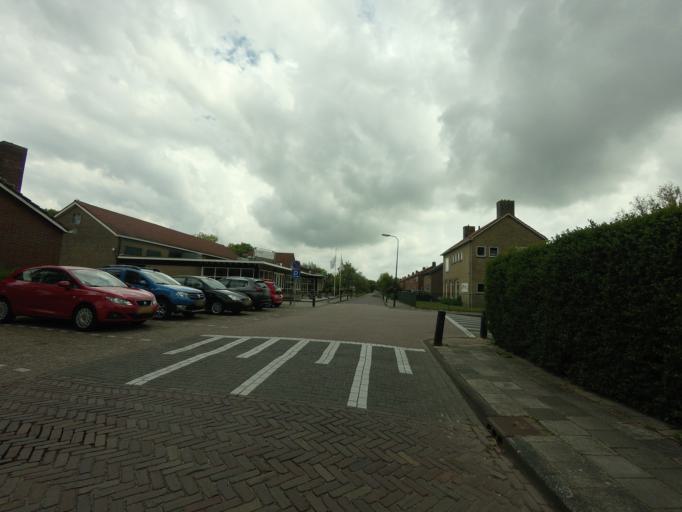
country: NL
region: Friesland
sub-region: Gemeente Littenseradiel
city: Wommels
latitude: 53.1081
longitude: 5.5896
